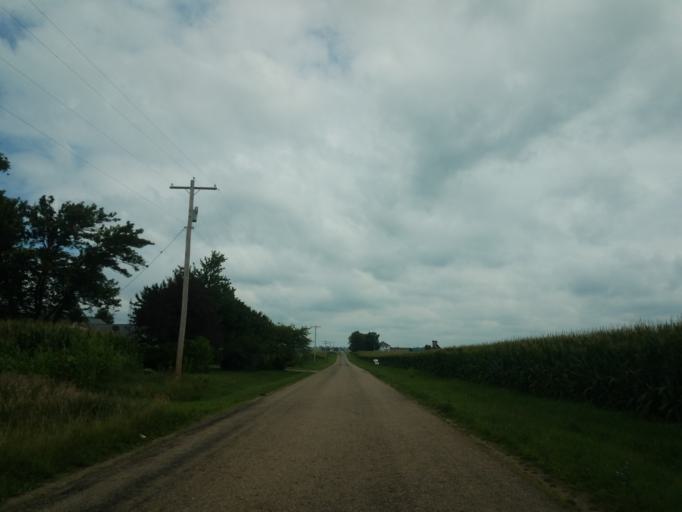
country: US
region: Illinois
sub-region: McLean County
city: Twin Grove
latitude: 40.4218
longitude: -89.0621
